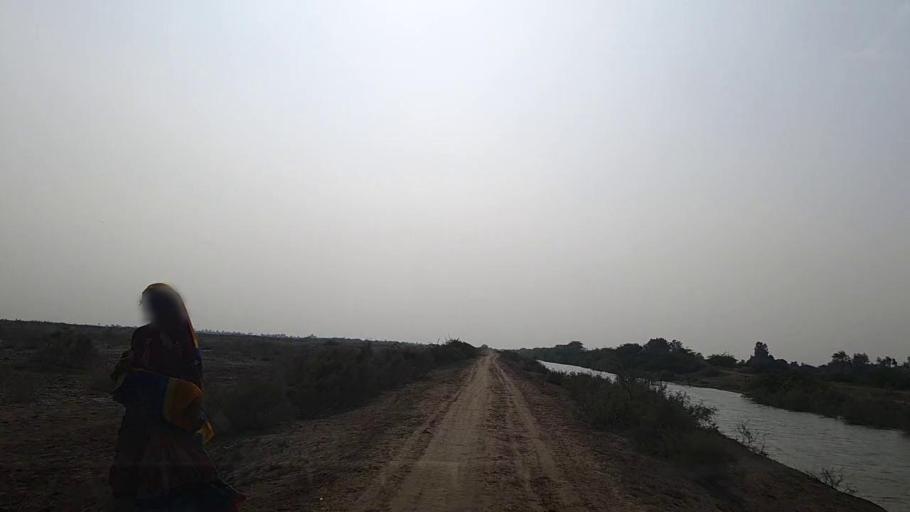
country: PK
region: Sindh
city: Gharo
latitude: 24.6649
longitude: 67.6324
